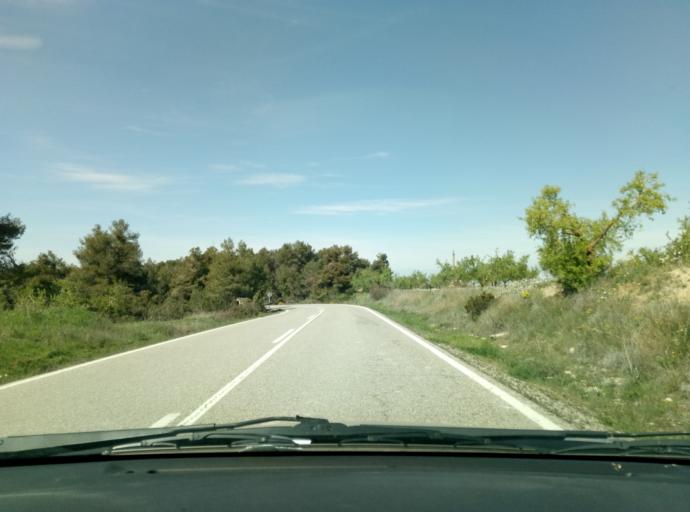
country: ES
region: Catalonia
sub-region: Provincia de Lleida
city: Fulleda
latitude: 41.5037
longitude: 1.0066
